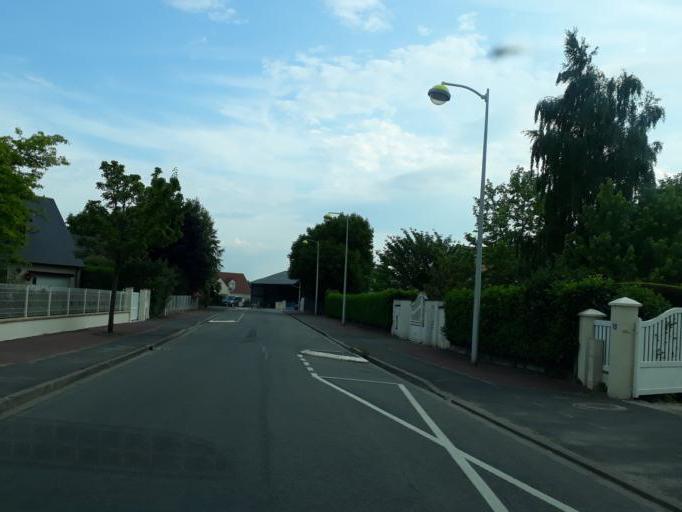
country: FR
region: Centre
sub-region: Departement du Loiret
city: Ormes
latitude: 47.9358
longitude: 1.8165
